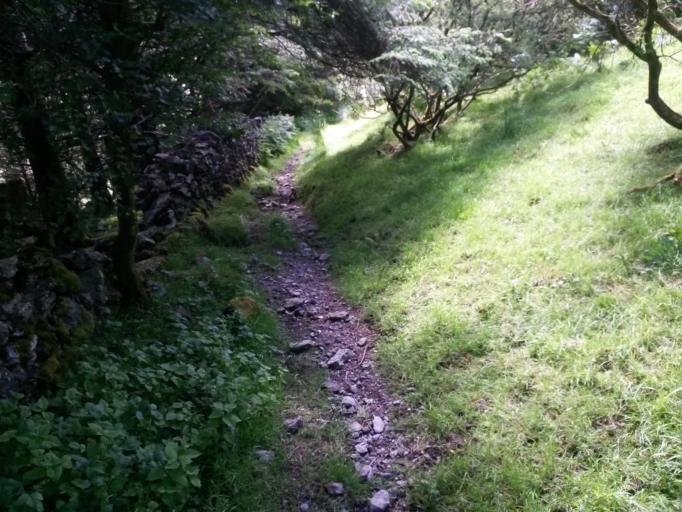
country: IE
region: Connaught
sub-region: Sligo
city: Strandhill
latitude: 54.2614
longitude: -8.5688
